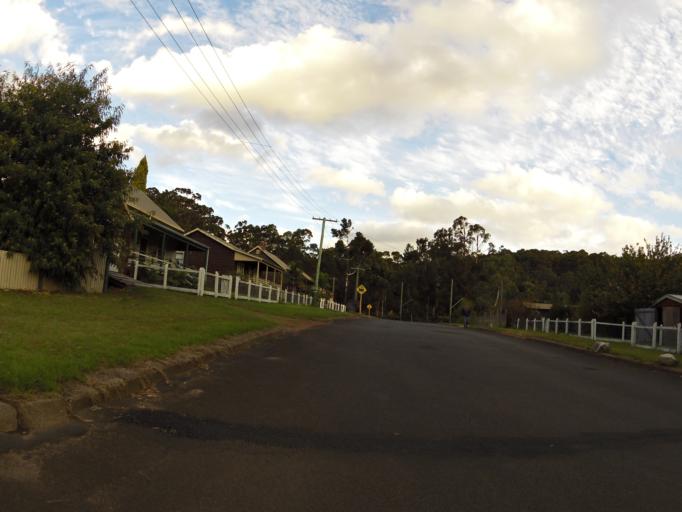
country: AU
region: Western Australia
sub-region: Manjimup
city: Pemberton
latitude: -34.4478
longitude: 116.0309
